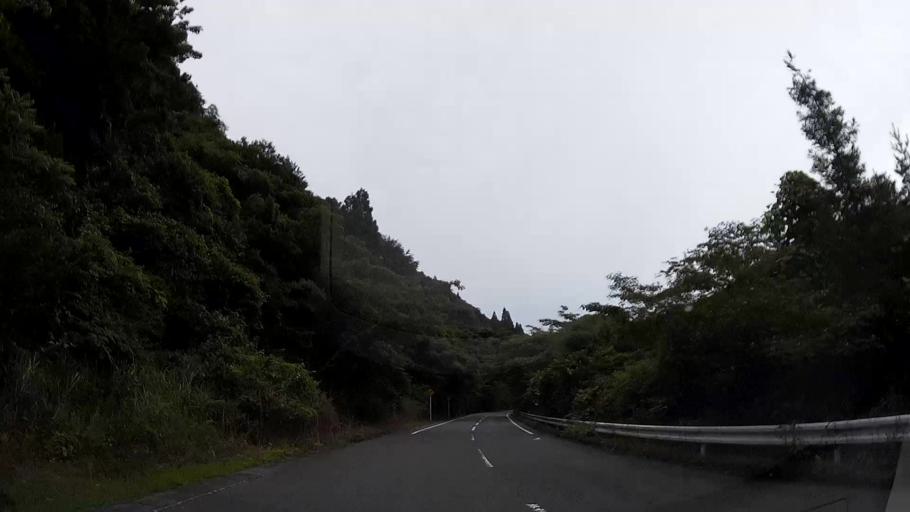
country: JP
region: Kumamoto
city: Kikuchi
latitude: 33.0583
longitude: 130.9025
